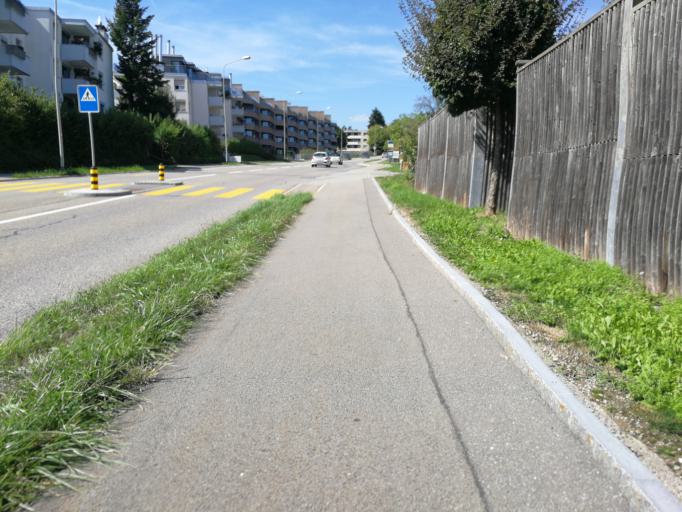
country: CH
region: Zurich
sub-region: Bezirk Horgen
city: Waedenswil / Hangenmoos
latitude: 47.2342
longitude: 8.6538
